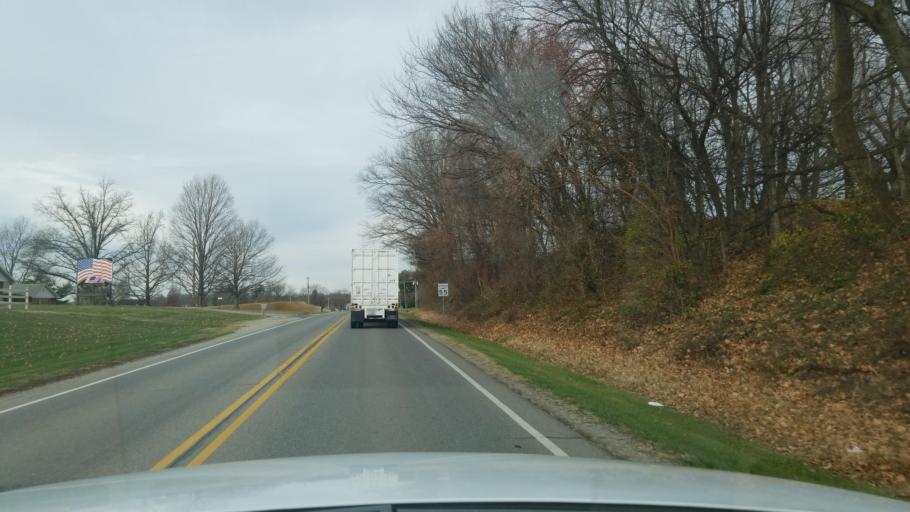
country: US
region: Indiana
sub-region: Posey County
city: Mount Vernon
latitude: 37.9291
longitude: -87.9356
